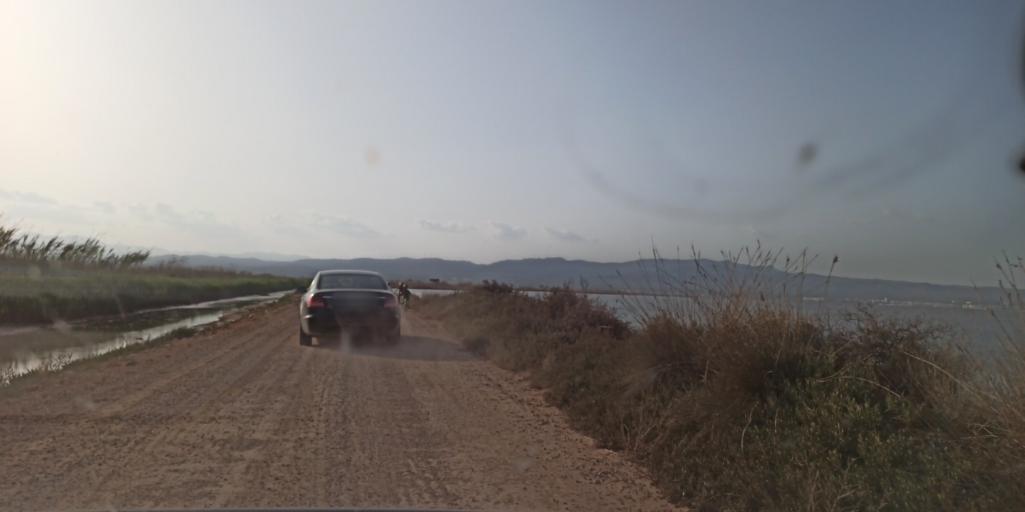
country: ES
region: Catalonia
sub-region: Provincia de Tarragona
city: L'Ampolla
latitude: 40.7684
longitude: 0.7330
